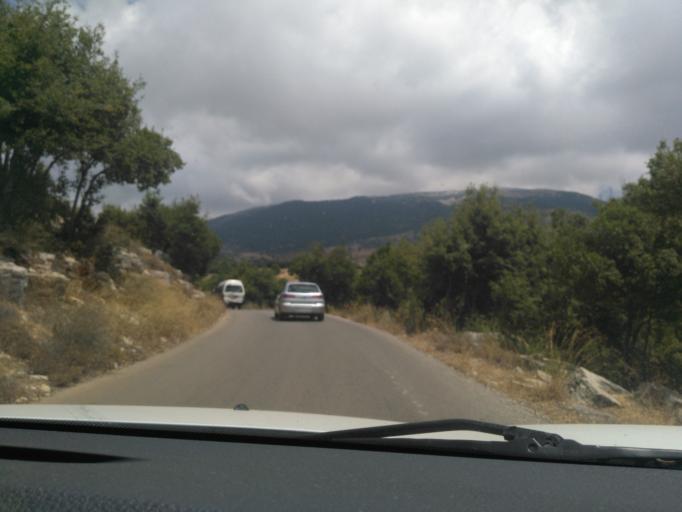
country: LB
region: Mont-Liban
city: Beit ed Dine
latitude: 33.6875
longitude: 35.6644
